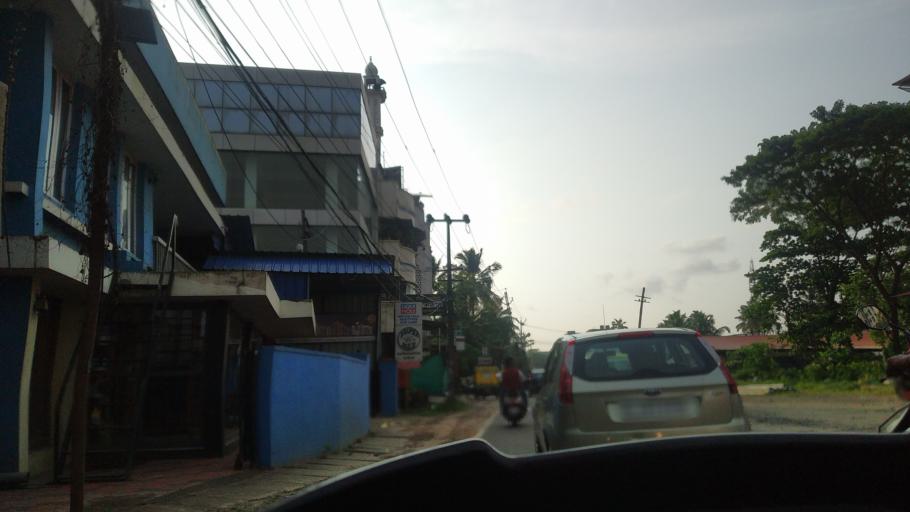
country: IN
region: Kerala
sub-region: Ernakulam
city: Cochin
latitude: 9.9833
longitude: 76.2981
